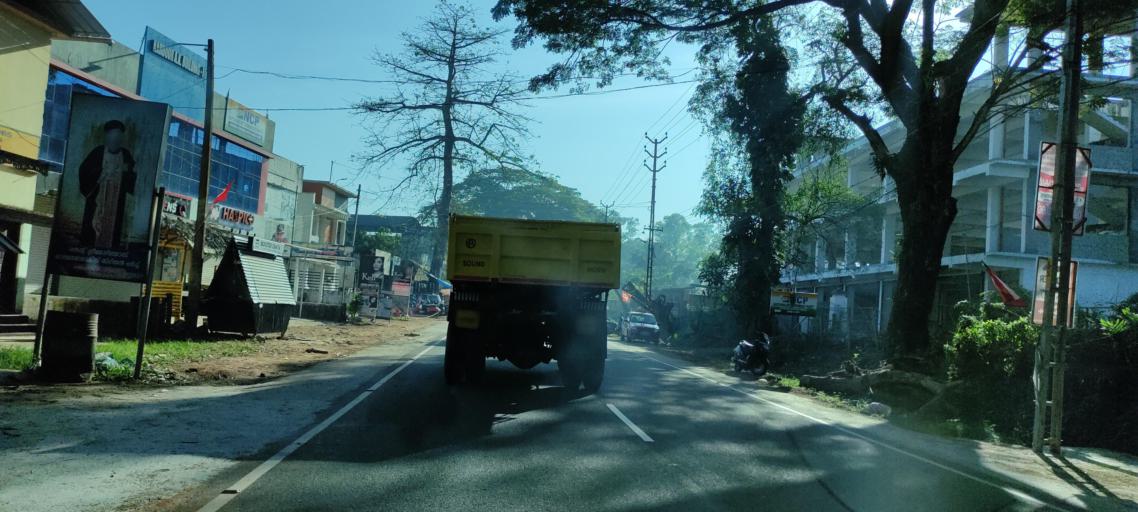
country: IN
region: Kerala
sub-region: Alappuzha
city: Kattanam
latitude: 9.1718
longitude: 76.5974
